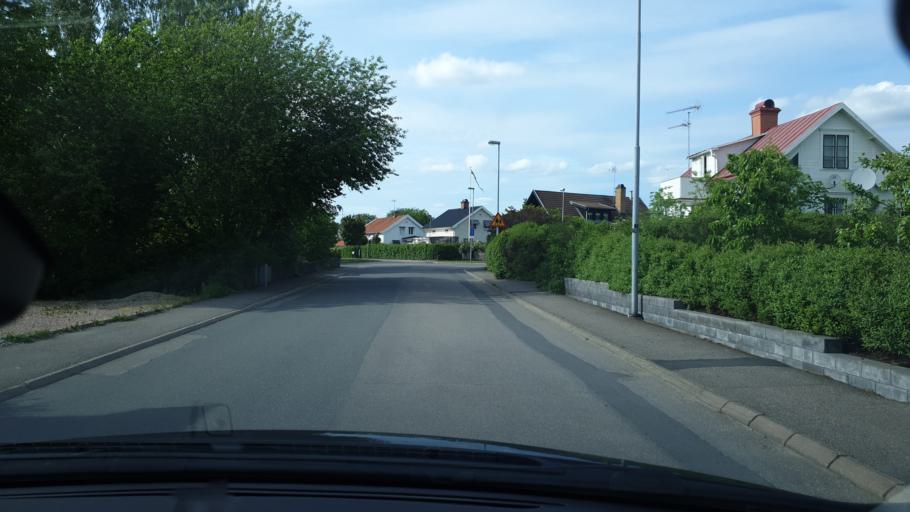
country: SE
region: Joenkoeping
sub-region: Vetlanda Kommun
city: Vetlanda
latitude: 57.4303
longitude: 15.0894
